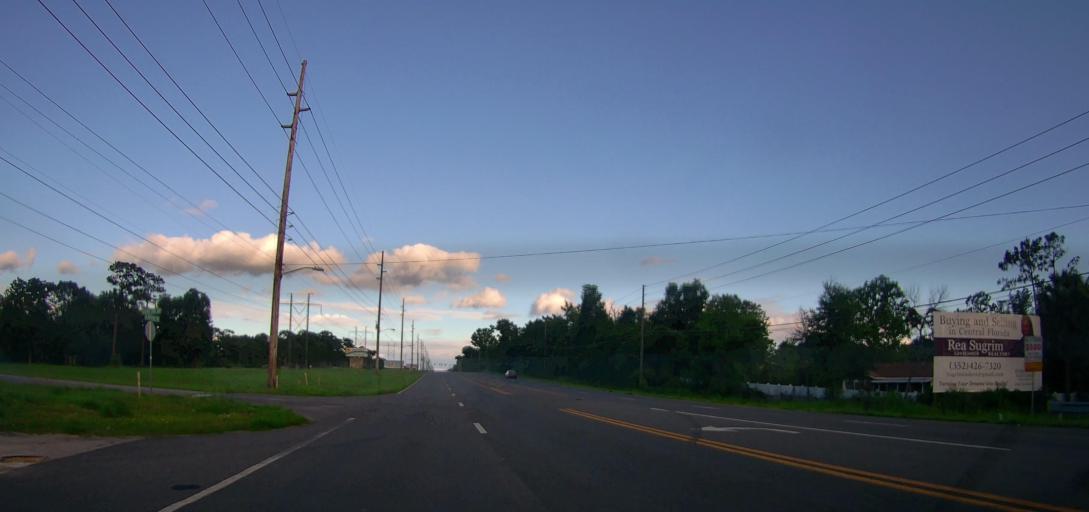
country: US
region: Florida
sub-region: Marion County
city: Silver Springs Shores
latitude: 29.1013
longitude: -82.0093
